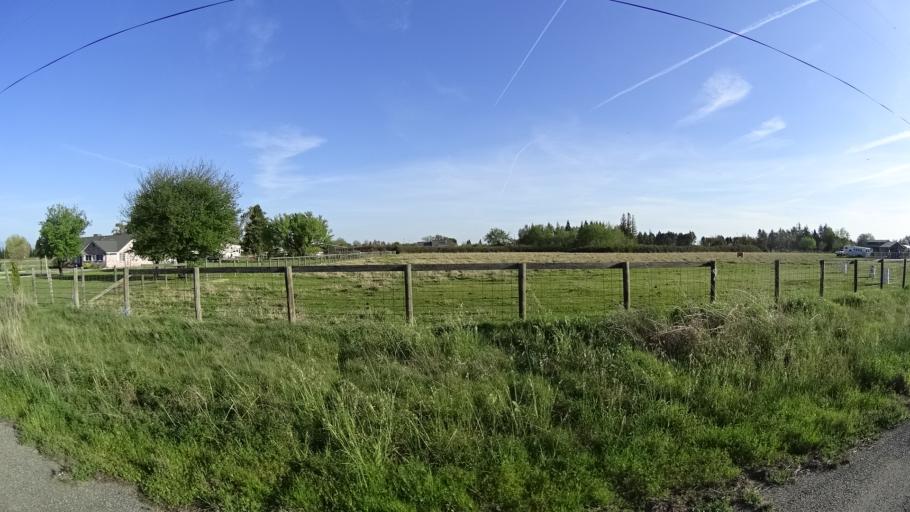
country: US
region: California
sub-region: Glenn County
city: Orland
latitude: 39.7331
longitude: -122.2212
